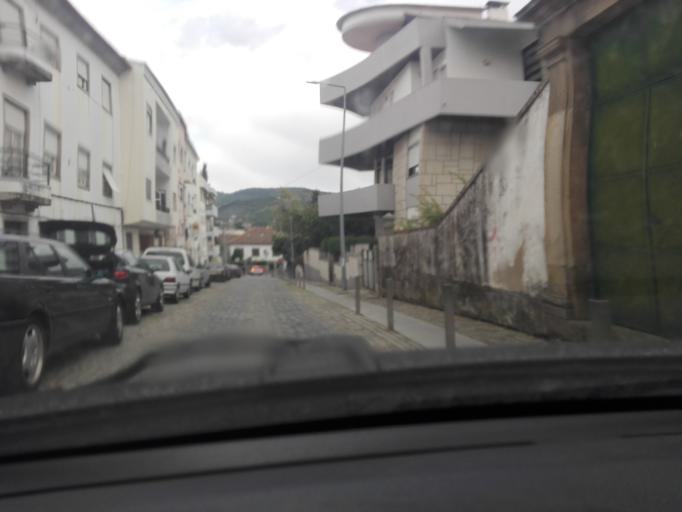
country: PT
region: Castelo Branco
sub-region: Concelho do Fundao
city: Fundao
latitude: 40.1377
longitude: -7.4987
